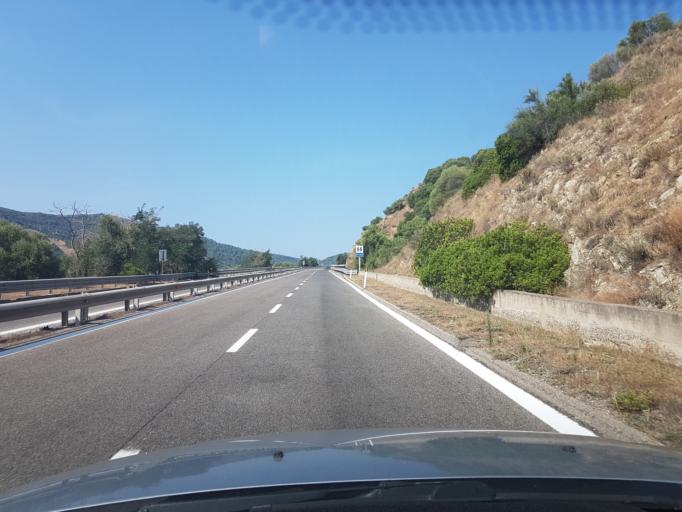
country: IT
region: Sardinia
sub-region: Provincia di Nuoro
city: Nuoro
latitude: 40.3460
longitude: 9.3251
